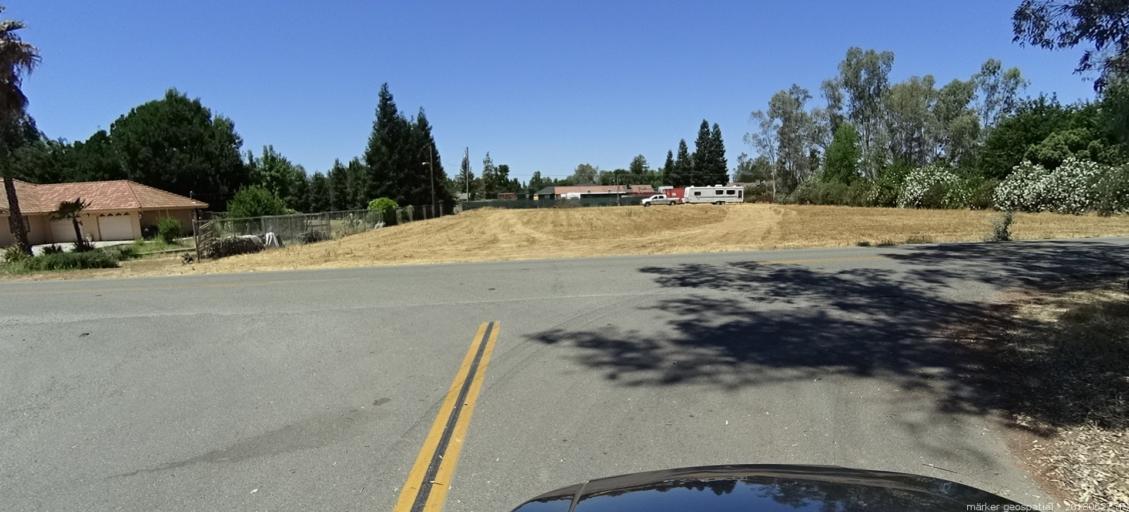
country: US
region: California
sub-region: Madera County
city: Bonadelle Ranchos-Madera Ranchos
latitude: 36.9322
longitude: -119.8670
